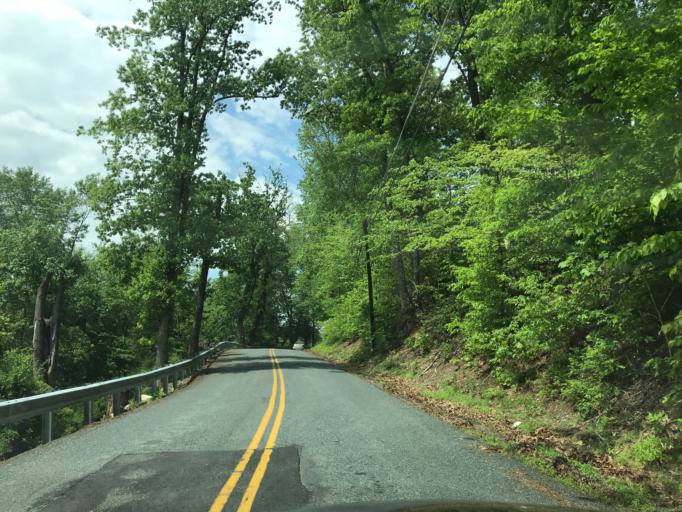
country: US
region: Maryland
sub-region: Harford County
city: Bel Air North
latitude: 39.6088
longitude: -76.3516
